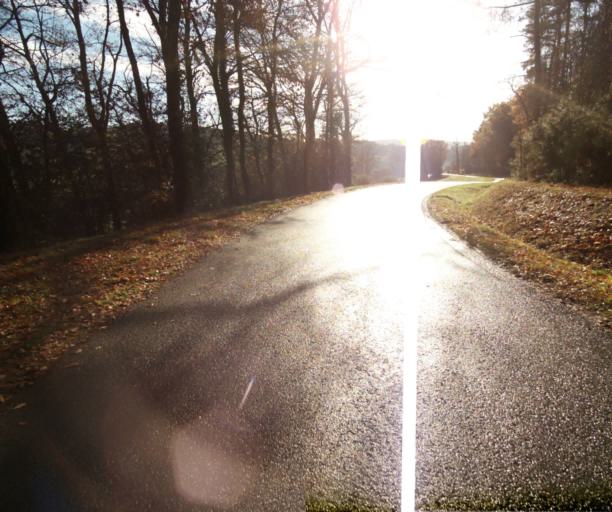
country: FR
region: Limousin
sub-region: Departement de la Correze
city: Saint-Mexant
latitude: 45.2415
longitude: 1.6372
